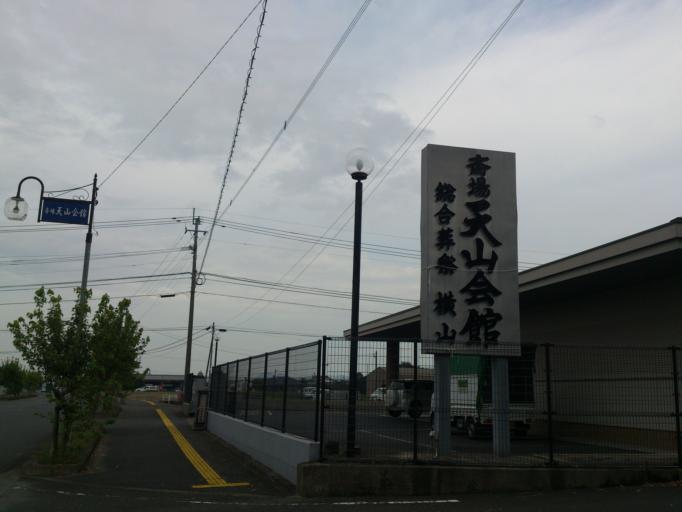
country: JP
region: Kagoshima
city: Kanoya
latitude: 31.3518
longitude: 130.9433
